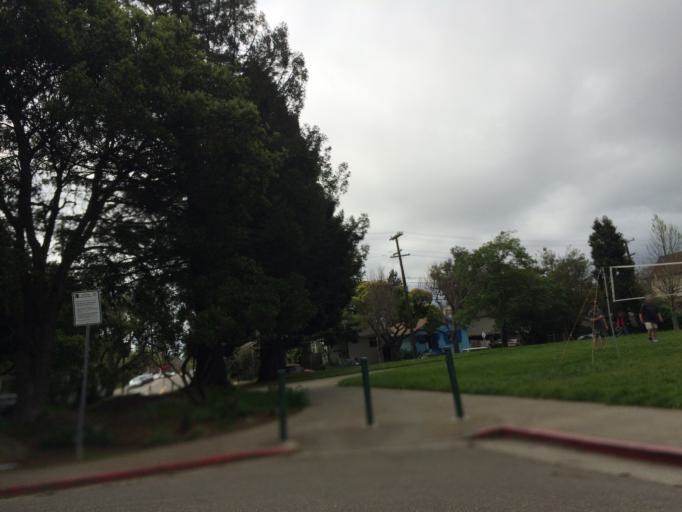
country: US
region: California
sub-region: Alameda County
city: Berkeley
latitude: 37.8730
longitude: -122.2801
